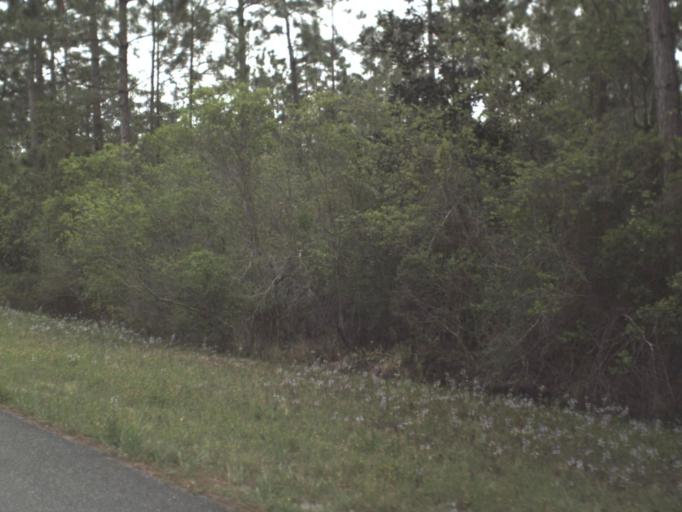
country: US
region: Florida
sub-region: Escambia County
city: Myrtle Grove
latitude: 30.4036
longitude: -87.3606
